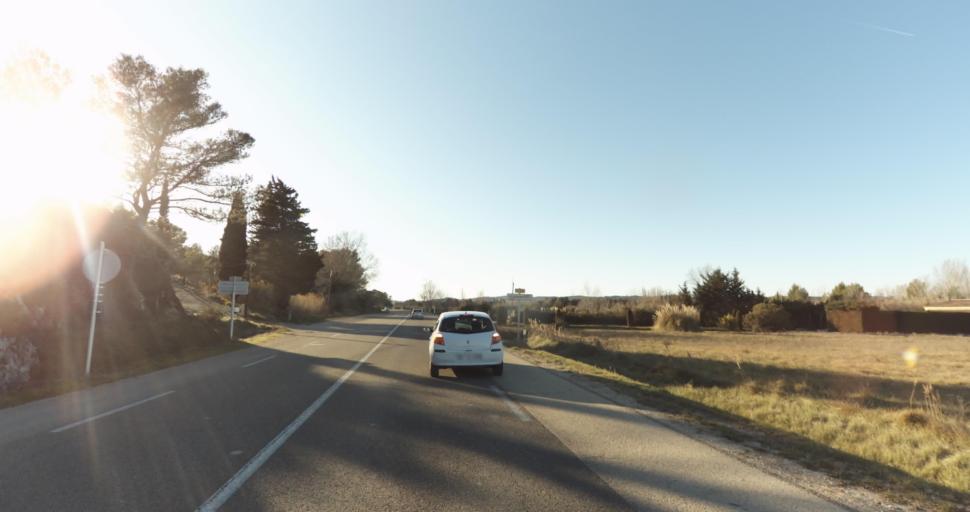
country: FR
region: Provence-Alpes-Cote d'Azur
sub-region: Departement des Bouches-du-Rhone
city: Barbentane
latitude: 43.8994
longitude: 4.7336
